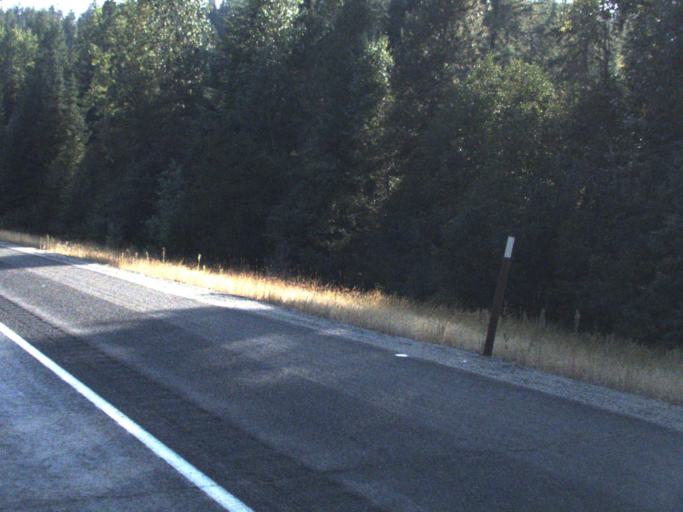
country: US
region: Washington
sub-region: Spokane County
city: Deer Park
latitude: 48.0908
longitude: -117.3260
